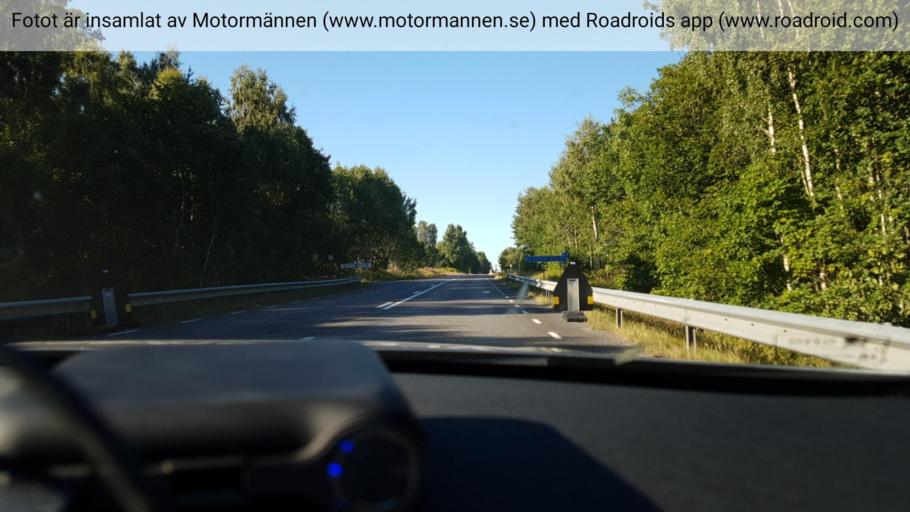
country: SE
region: Joenkoeping
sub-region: Habo Kommun
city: Habo
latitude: 57.9408
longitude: 14.0990
